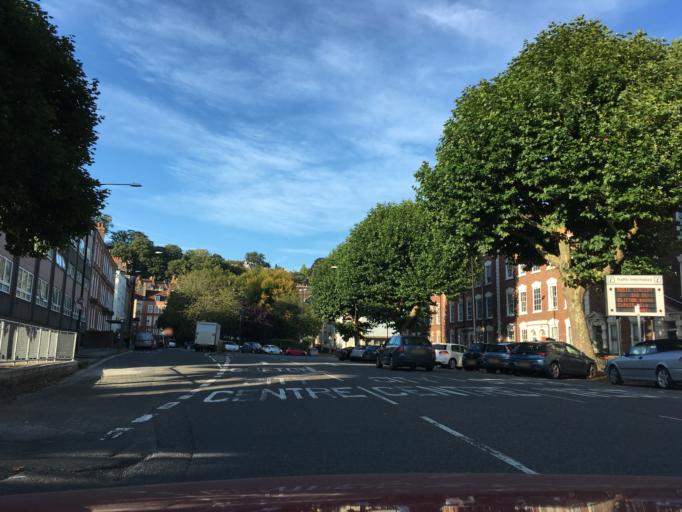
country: GB
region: England
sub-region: Bristol
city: Bristol
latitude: 51.4500
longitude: -2.6211
